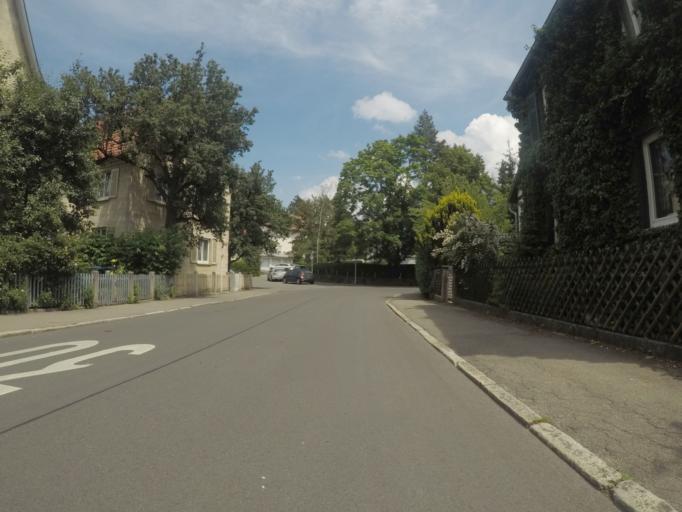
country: DE
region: Baden-Wuerttemberg
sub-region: Tuebingen Region
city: Reutlingen
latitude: 48.4821
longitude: 9.2149
